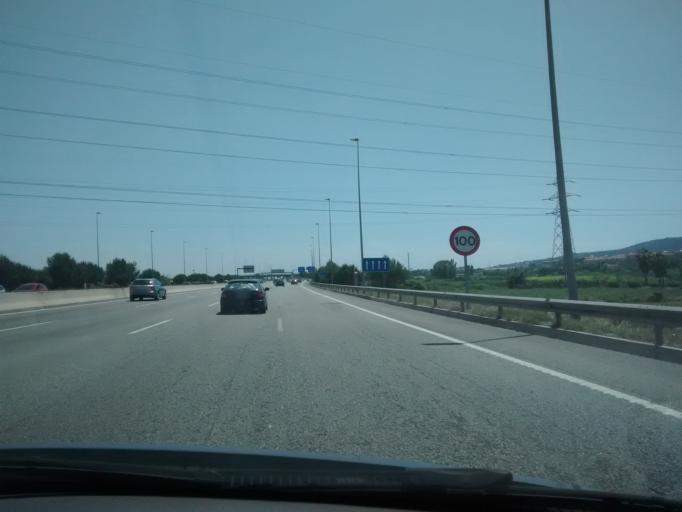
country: ES
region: Catalonia
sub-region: Provincia de Barcelona
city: Sant Vicenc dels Horts
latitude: 41.3856
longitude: 2.0215
